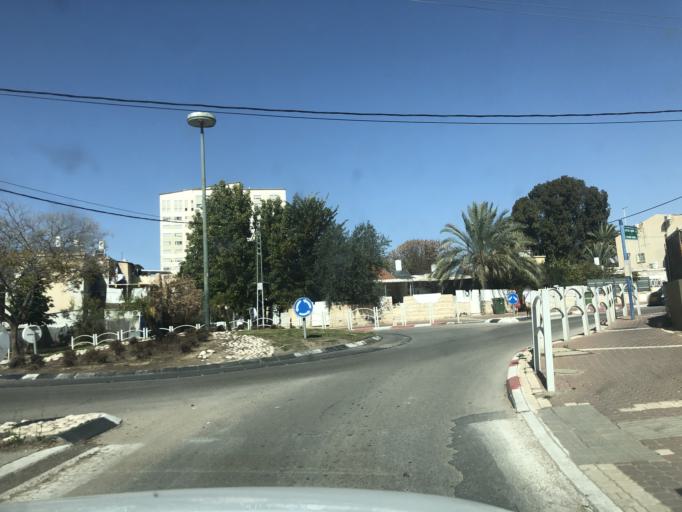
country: IL
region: Southern District
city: Beersheba
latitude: 31.2617
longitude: 34.7952
